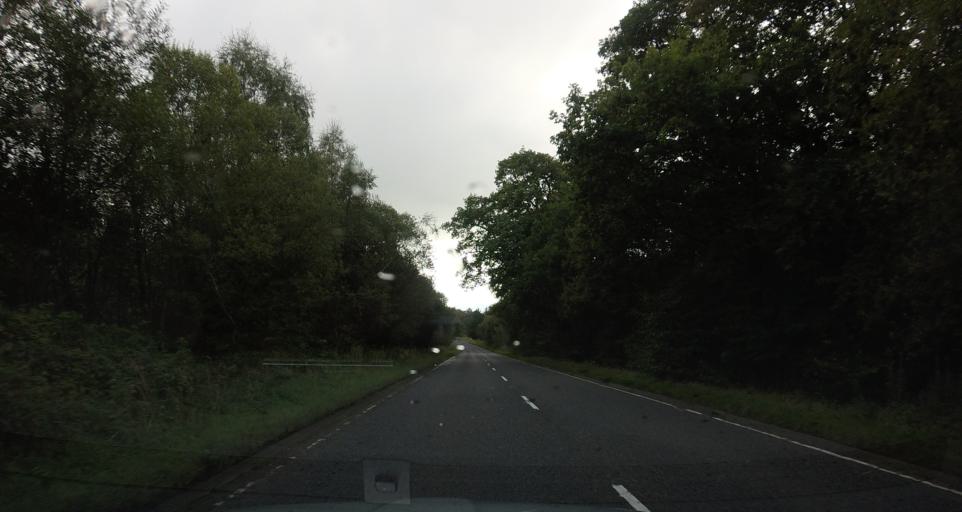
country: GB
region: Scotland
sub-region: Fife
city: Saline
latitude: 56.1612
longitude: -3.6026
